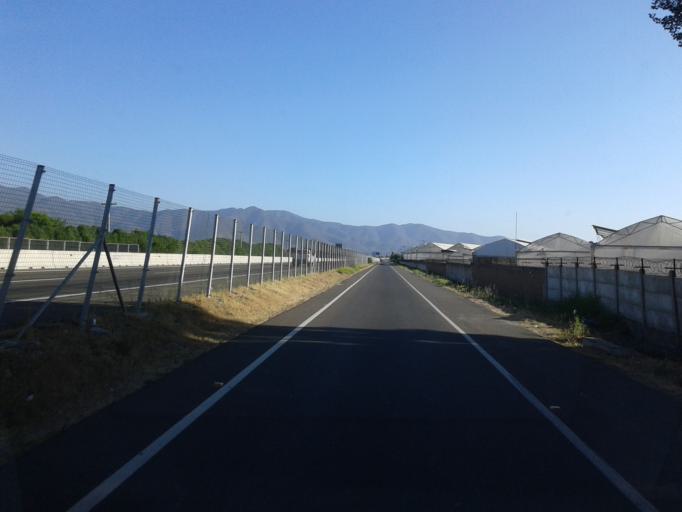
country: CL
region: Valparaiso
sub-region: Provincia de Quillota
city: Quillota
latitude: -32.8496
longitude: -71.2245
